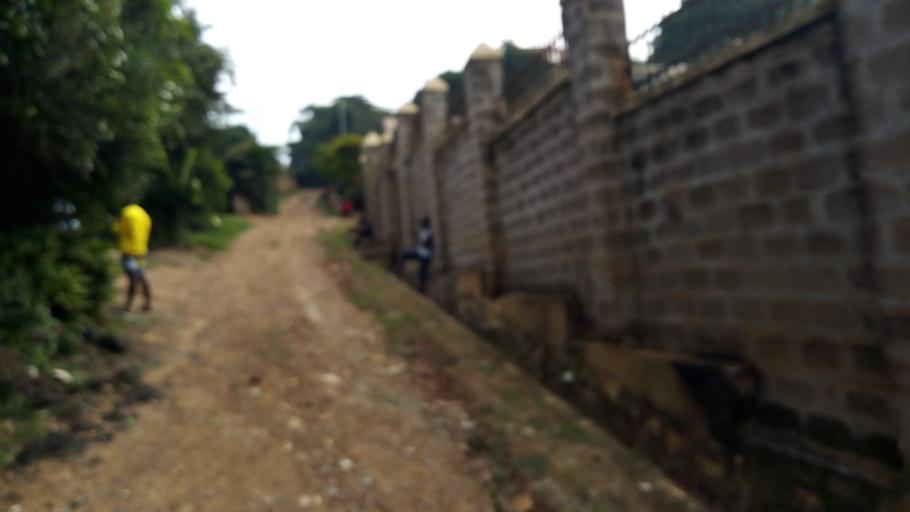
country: UG
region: Central Region
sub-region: Wakiso District
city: Kireka
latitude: 0.3141
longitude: 32.6480
